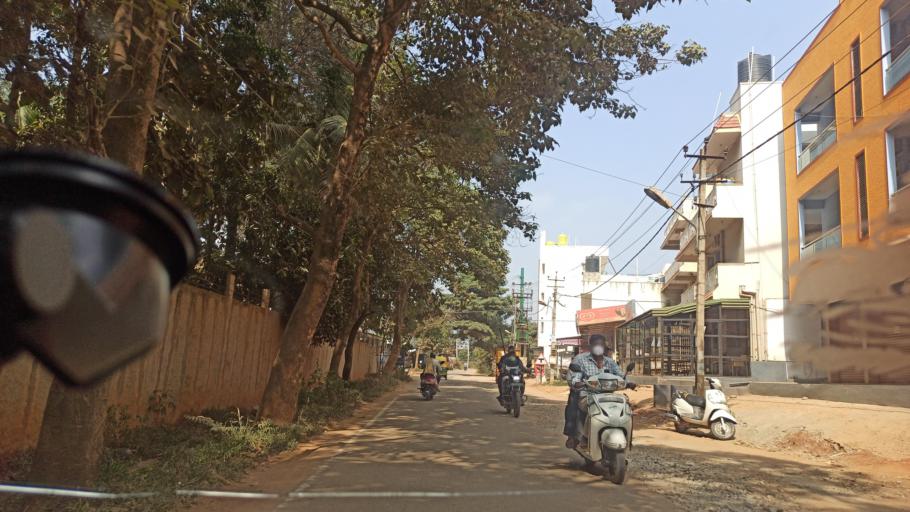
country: IN
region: Karnataka
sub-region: Bangalore Urban
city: Yelahanka
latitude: 13.0941
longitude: 77.6187
